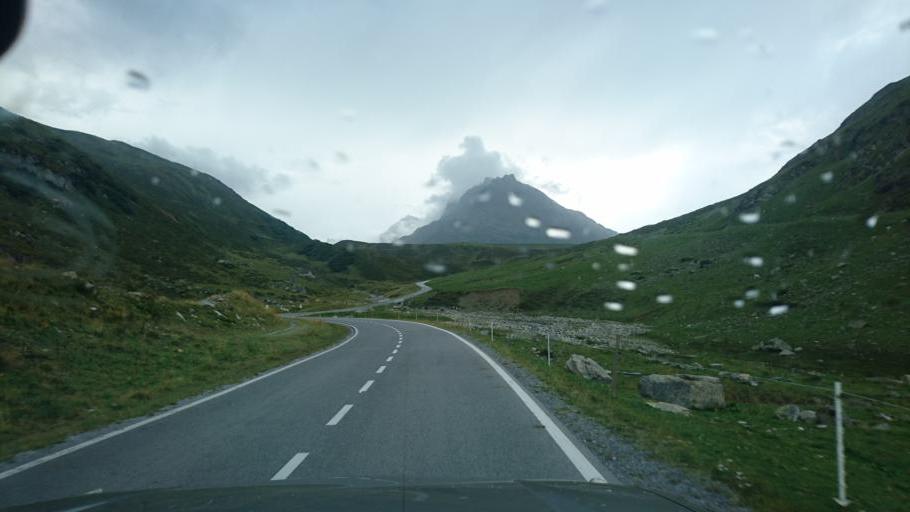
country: AT
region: Tyrol
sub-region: Politischer Bezirk Landeck
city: Galtur
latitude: 46.9218
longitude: 10.1145
